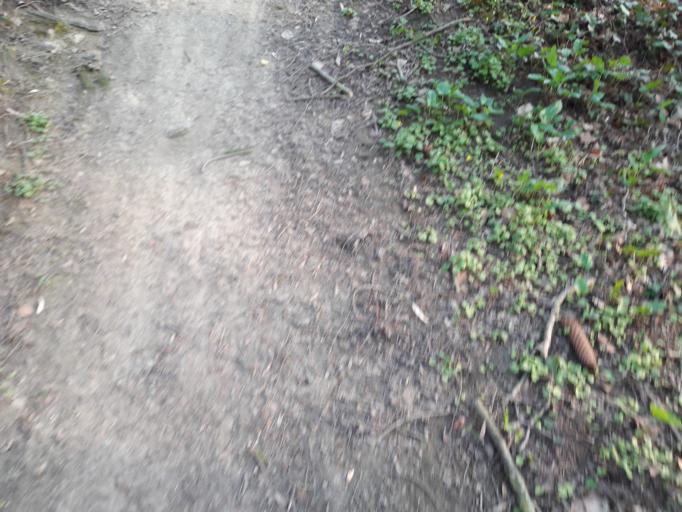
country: FR
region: Nord-Pas-de-Calais
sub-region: Departement du Nord
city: Boussois
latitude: 50.2866
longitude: 4.0415
